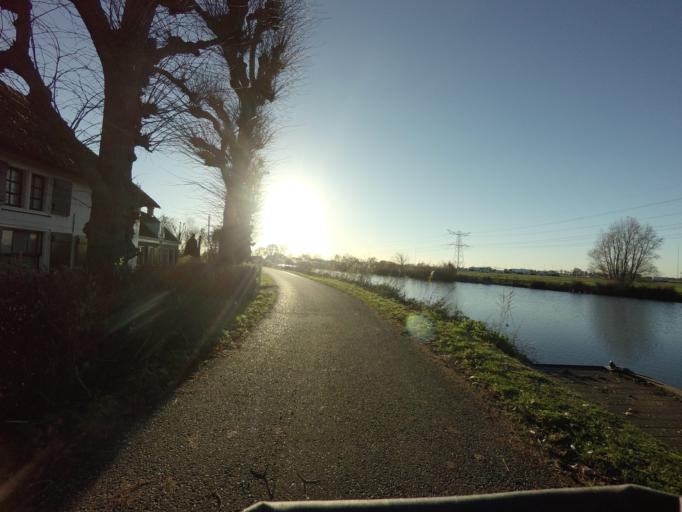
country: NL
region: Utrecht
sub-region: Stichtse Vecht
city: Breukelen
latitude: 52.2103
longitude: 4.9901
